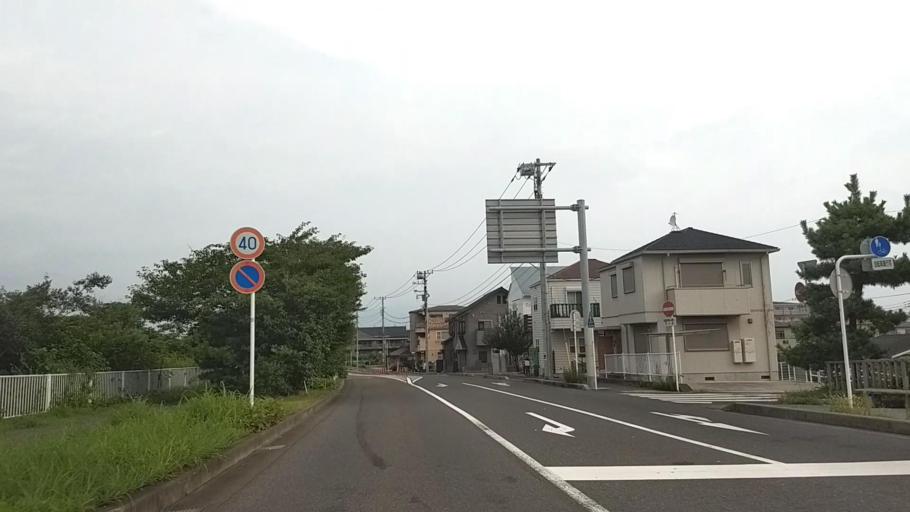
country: JP
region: Kanagawa
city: Hiratsuka
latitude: 35.3238
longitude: 139.3294
